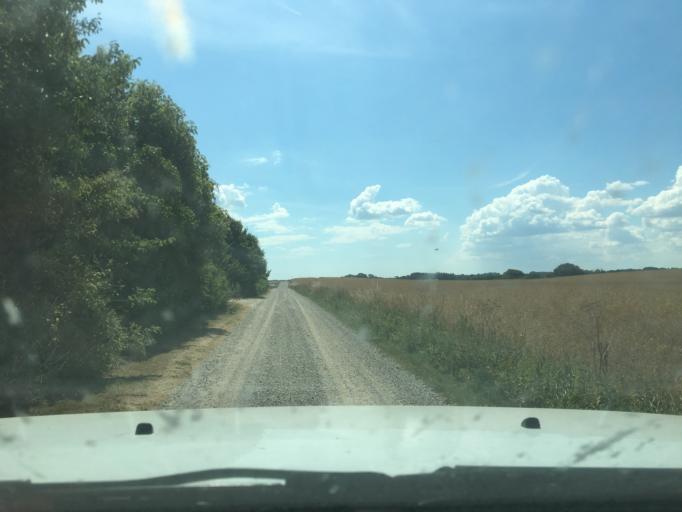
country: DK
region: Central Jutland
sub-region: Arhus Kommune
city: Trige
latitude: 56.3467
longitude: 10.1882
